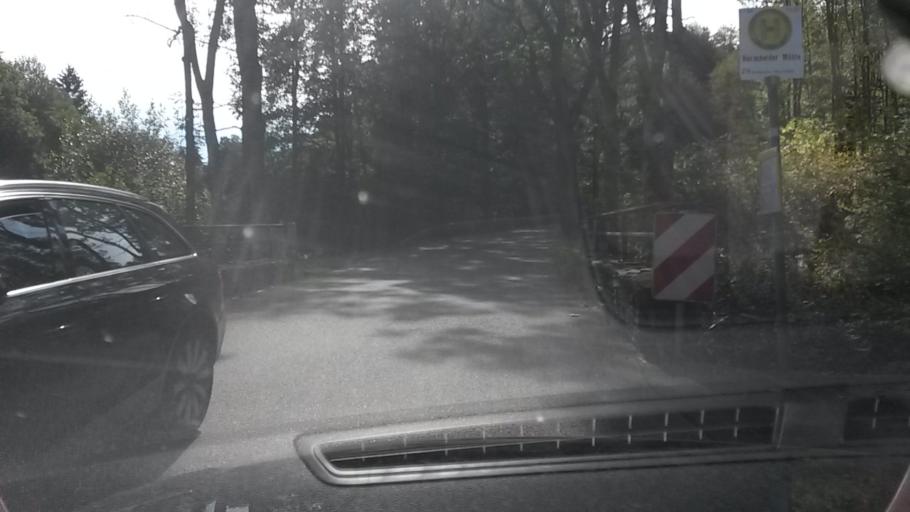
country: DE
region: North Rhine-Westphalia
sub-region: Regierungsbezirk Arnsberg
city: Herscheid
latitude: 51.1901
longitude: 7.7131
